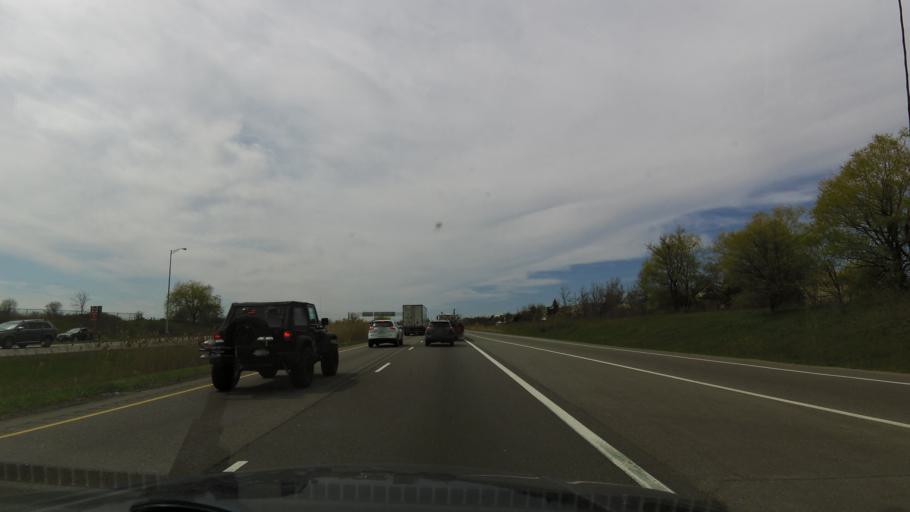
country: CA
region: Ontario
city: Oakville
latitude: 43.5141
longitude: -79.6966
